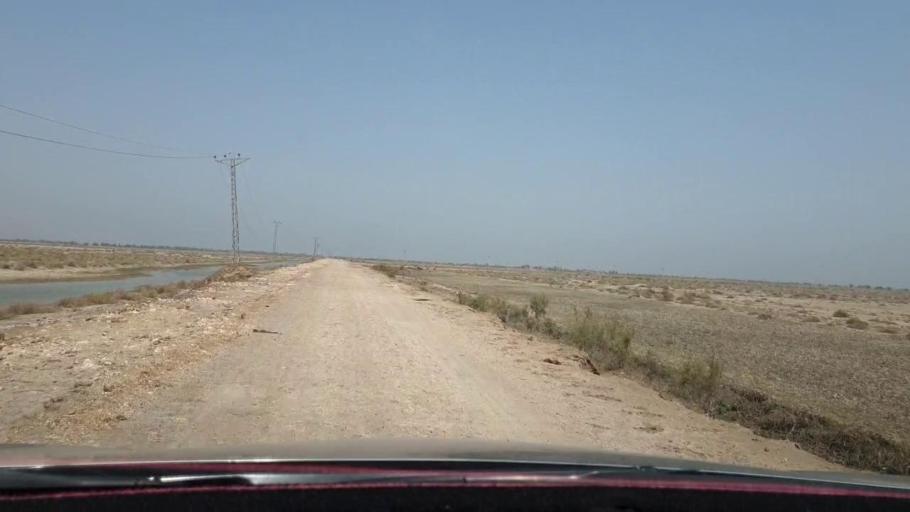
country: PK
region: Sindh
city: Warah
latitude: 27.3816
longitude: 67.6774
